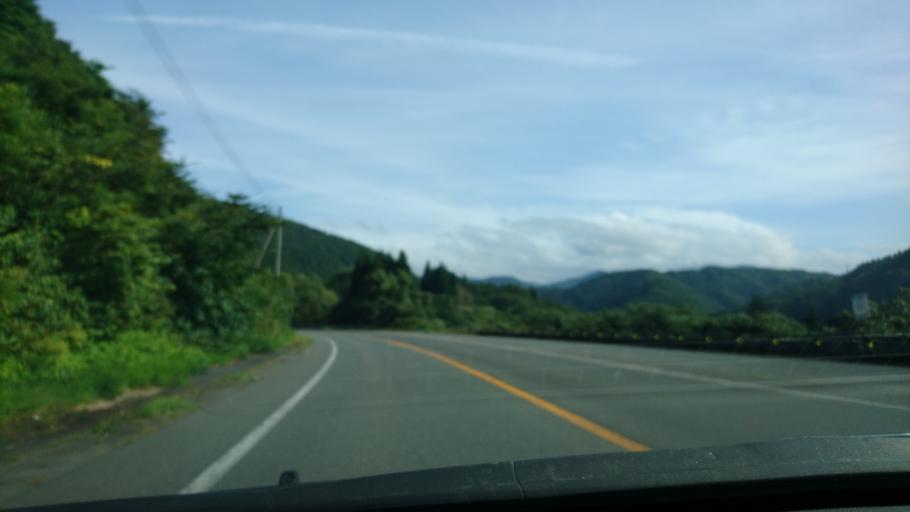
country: JP
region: Akita
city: Yokotemachi
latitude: 39.3135
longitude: 140.8019
